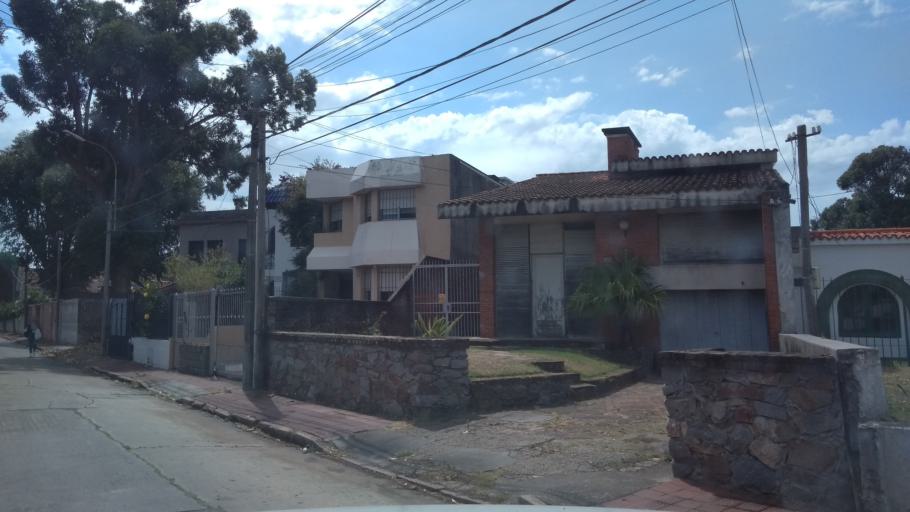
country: UY
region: Canelones
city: Paso de Carrasco
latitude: -34.8946
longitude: -56.0660
